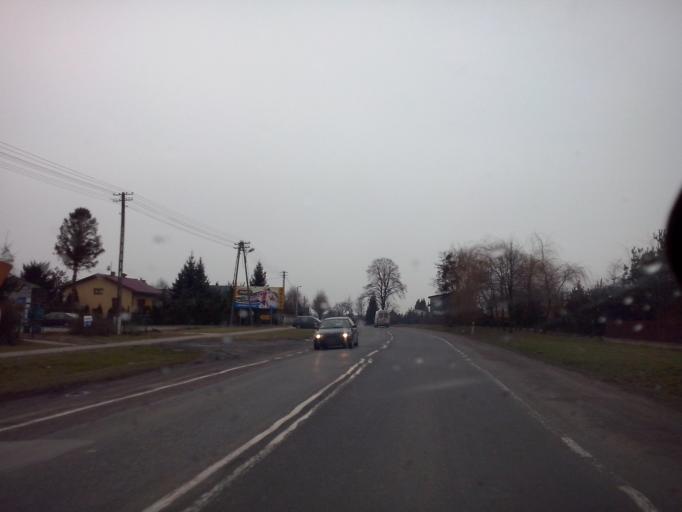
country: PL
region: Lublin Voivodeship
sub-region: Powiat zamojski
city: Michalow
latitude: 50.7236
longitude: 23.0994
